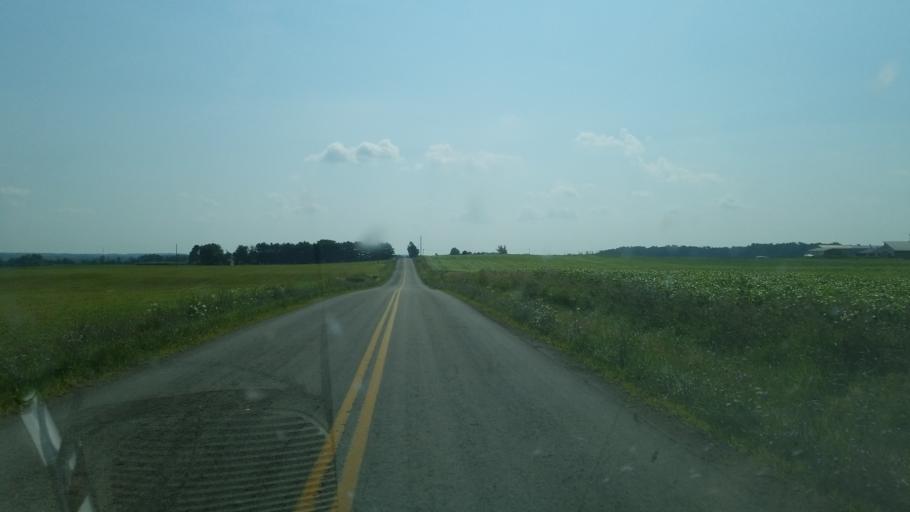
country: US
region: Ohio
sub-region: Huron County
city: Greenwich
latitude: 40.9533
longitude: -82.4144
